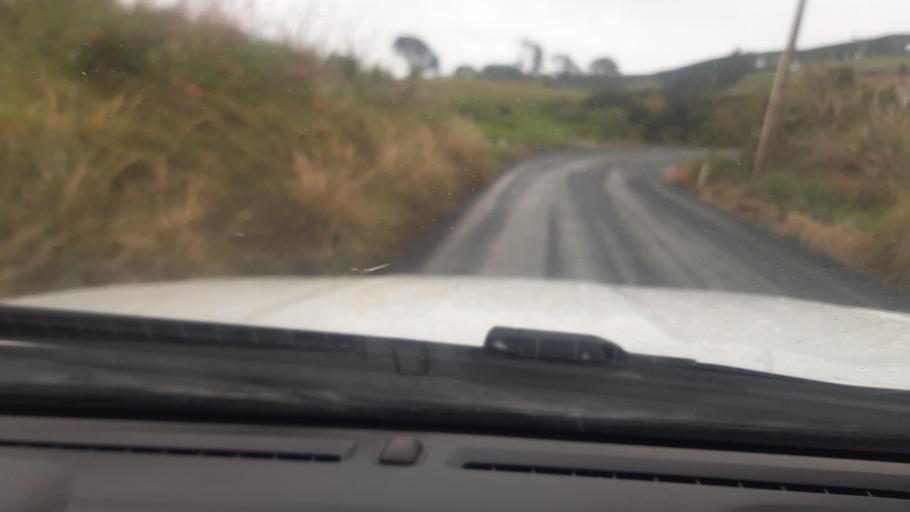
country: NZ
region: Northland
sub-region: Far North District
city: Kaitaia
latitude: -34.9798
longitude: 173.1964
